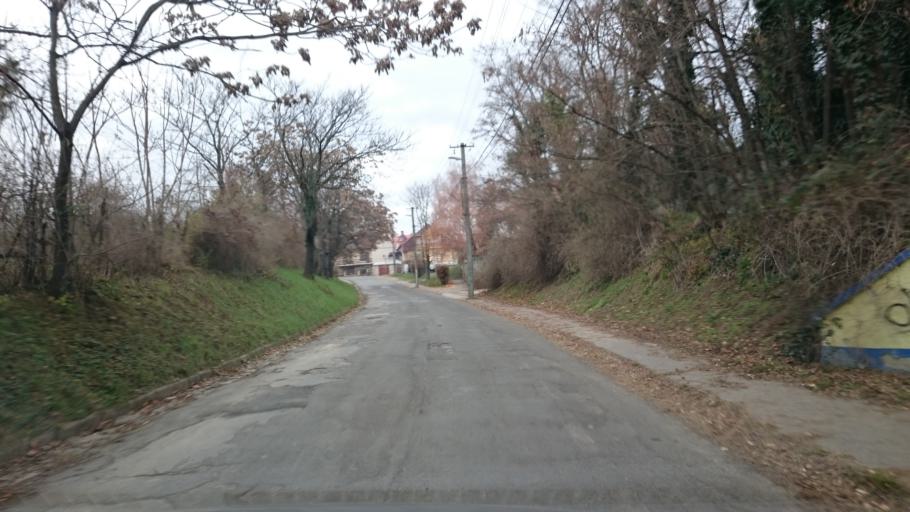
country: HU
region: Baranya
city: Pellerd
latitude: 46.0674
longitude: 18.1842
